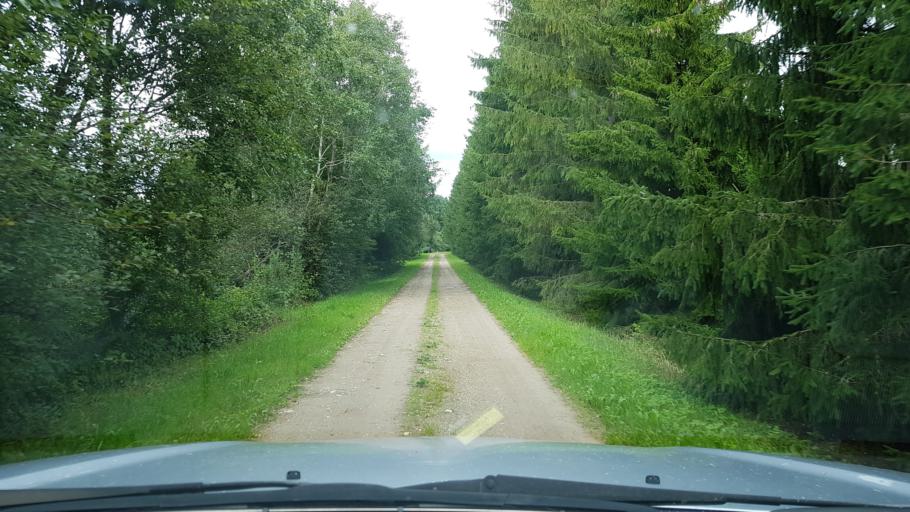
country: EE
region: Harju
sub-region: Rae vald
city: Vaida
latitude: 59.3644
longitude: 24.9819
